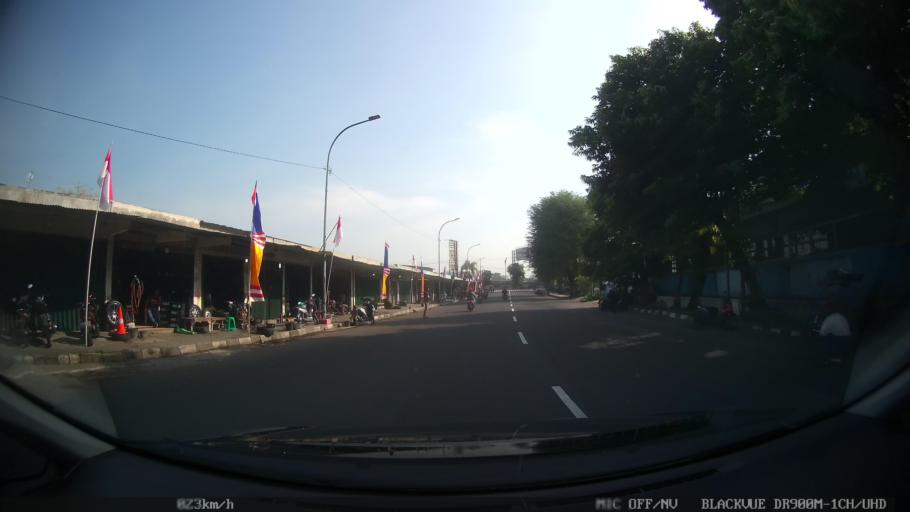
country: ID
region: Daerah Istimewa Yogyakarta
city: Yogyakarta
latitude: -7.7841
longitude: 110.3713
